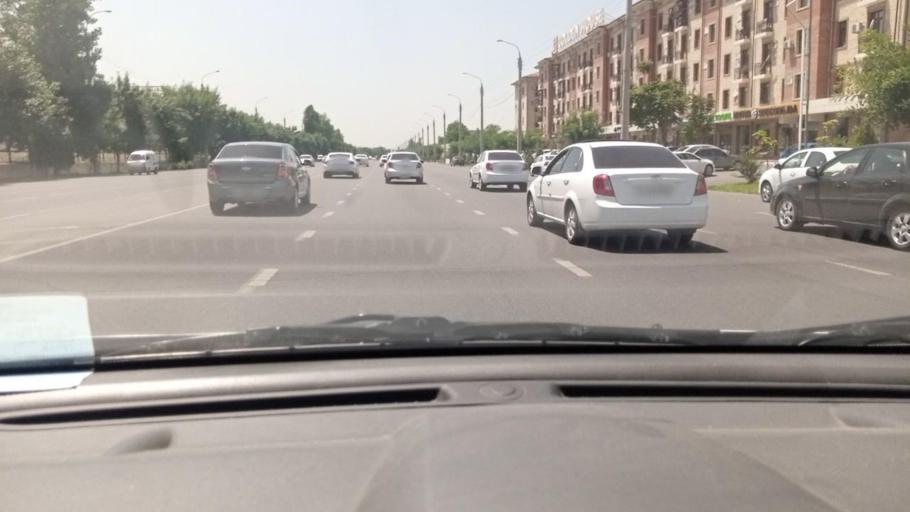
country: UZ
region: Toshkent Shahri
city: Tashkent
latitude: 41.2776
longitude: 69.2722
